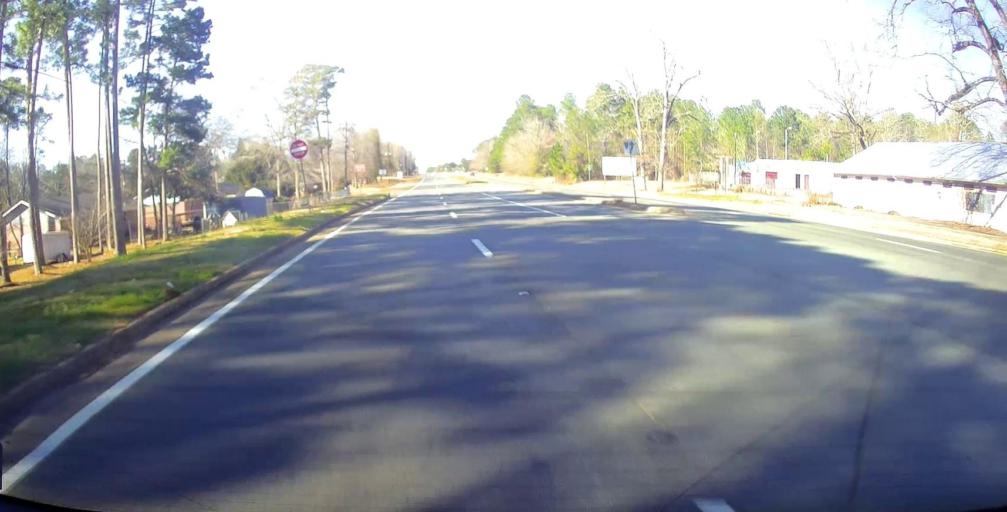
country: US
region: Georgia
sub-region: Sumter County
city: Americus
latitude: 32.0923
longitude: -84.2412
